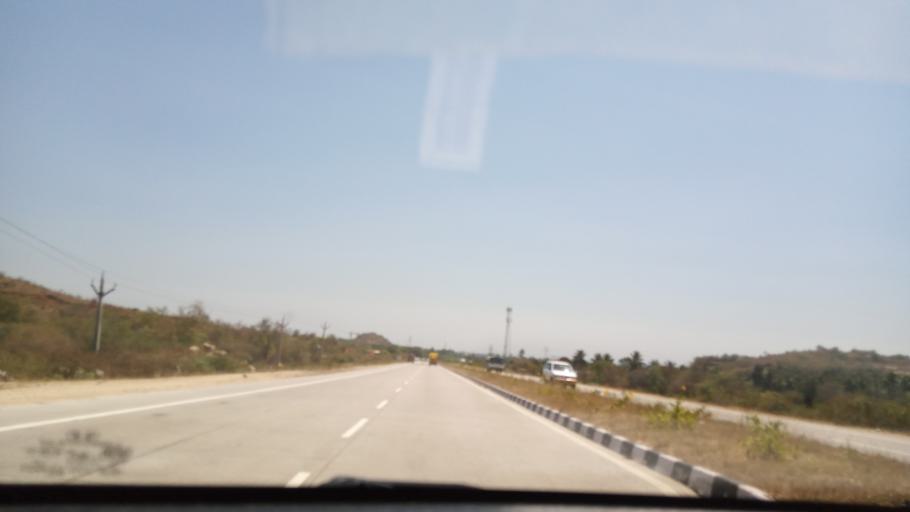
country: IN
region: Andhra Pradesh
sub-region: Chittoor
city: Chittoor
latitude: 13.2013
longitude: 78.9650
